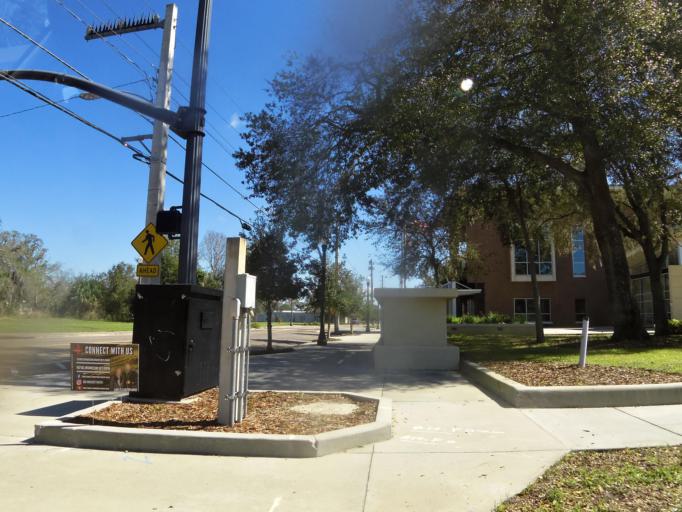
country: US
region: Florida
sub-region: Seminole County
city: Sanford
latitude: 28.8007
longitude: -81.2772
